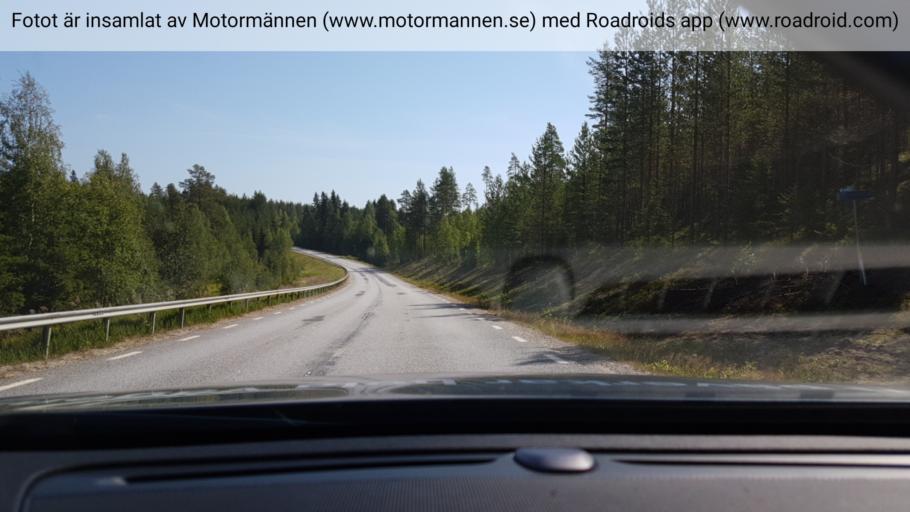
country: SE
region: Vaesterbotten
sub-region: Vindelns Kommun
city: Vindeln
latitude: 64.2437
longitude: 19.6613
